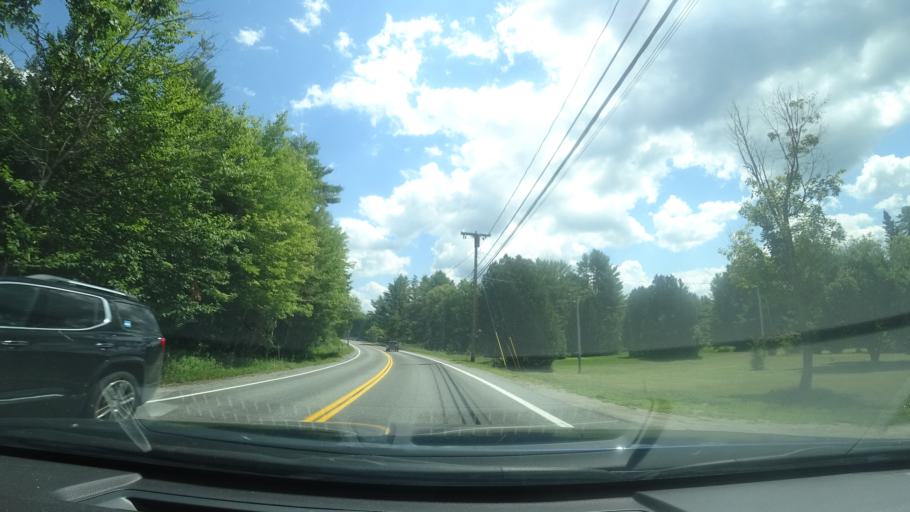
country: US
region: New York
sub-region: Warren County
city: Warrensburg
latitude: 43.6643
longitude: -73.8276
